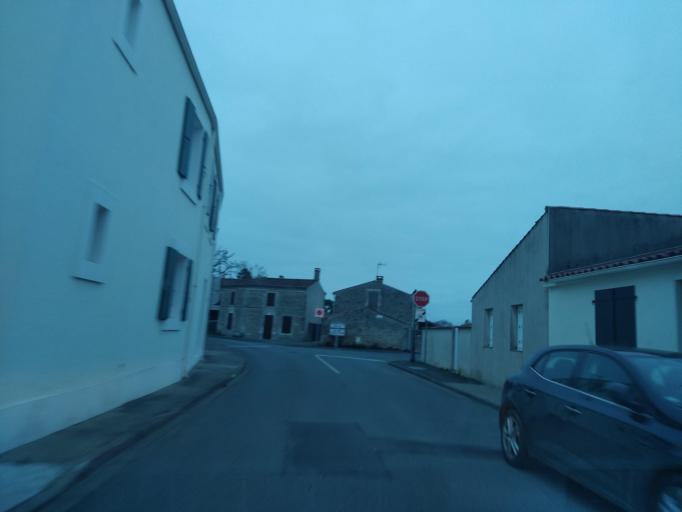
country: FR
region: Pays de la Loire
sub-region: Departement de la Vendee
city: Triaize
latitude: 46.3569
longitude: -1.2491
